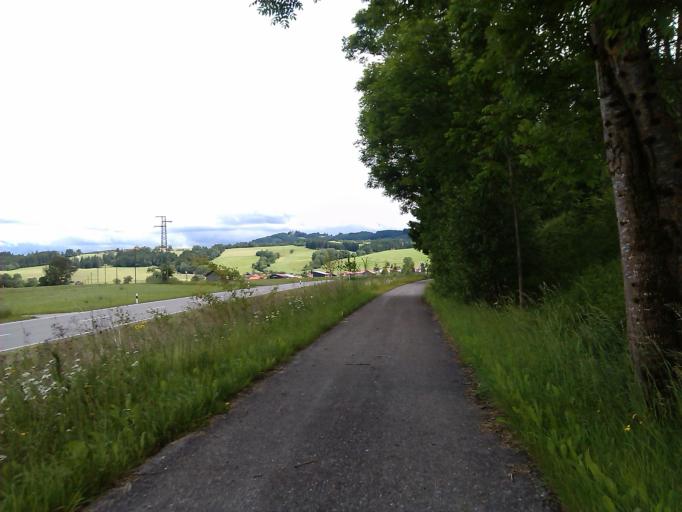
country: DE
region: Bavaria
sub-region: Swabia
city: Stotten am Auerberg
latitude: 47.7465
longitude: 10.6745
